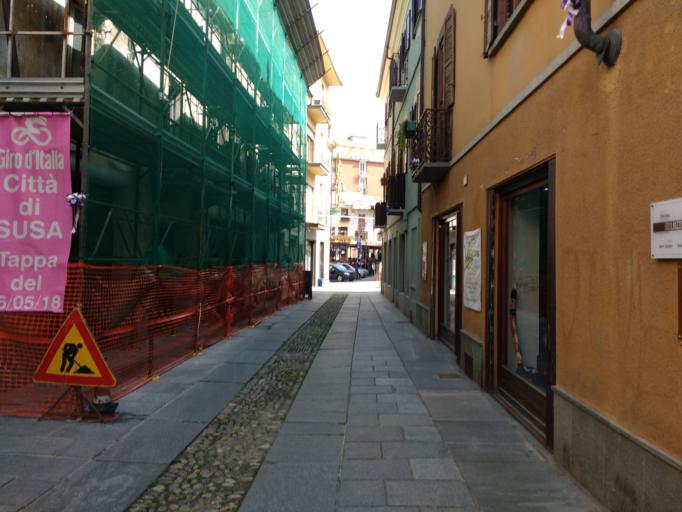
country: IT
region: Piedmont
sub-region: Provincia di Torino
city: Susa
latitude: 45.1360
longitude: 7.0469
